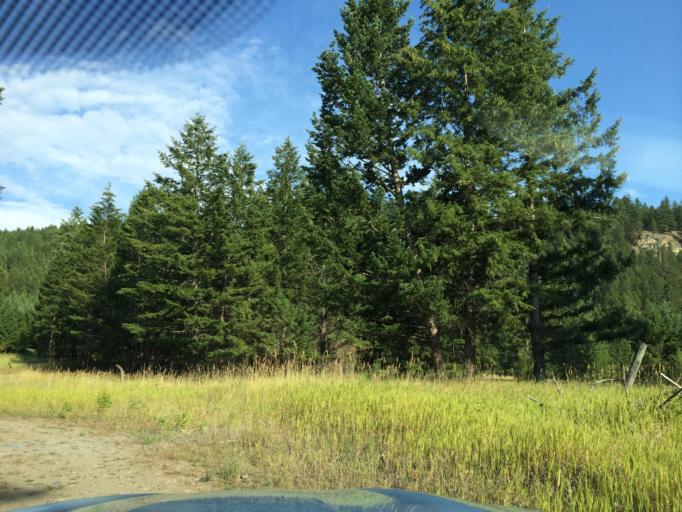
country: US
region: Montana
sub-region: Lincoln County
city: Eureka
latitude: 48.9997
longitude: -115.0518
